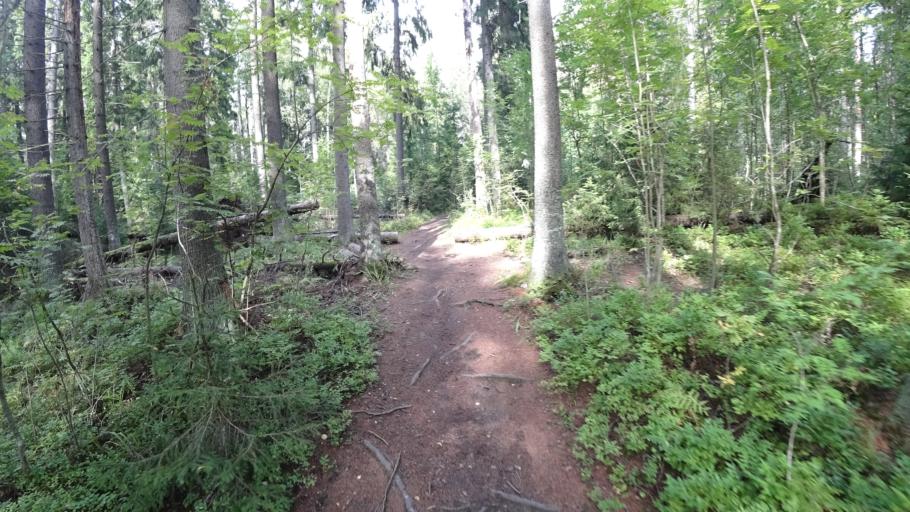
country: FI
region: Uusimaa
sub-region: Helsinki
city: Helsinki
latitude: 60.2595
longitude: 24.9199
